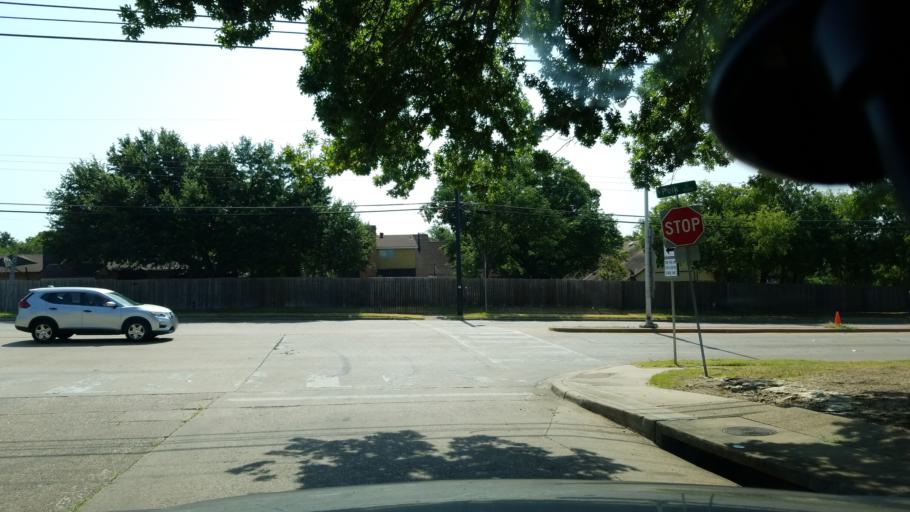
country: US
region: Texas
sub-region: Dallas County
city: Cockrell Hill
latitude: 32.6798
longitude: -96.8403
